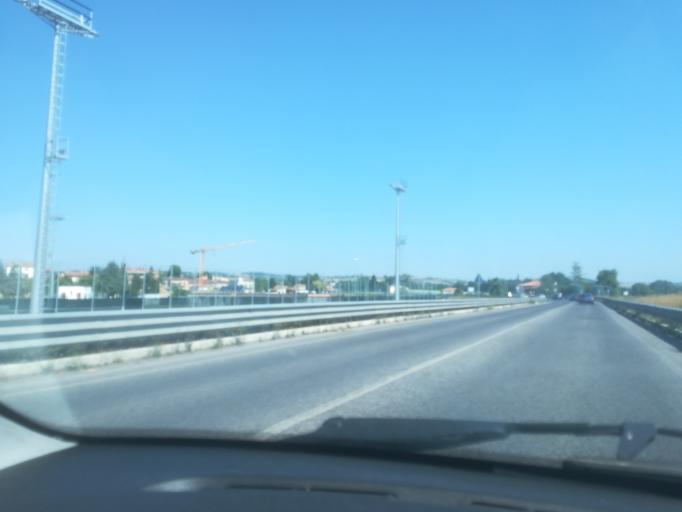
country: IT
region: The Marches
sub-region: Provincia di Macerata
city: Villa Potenza
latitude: 43.3231
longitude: 13.4295
